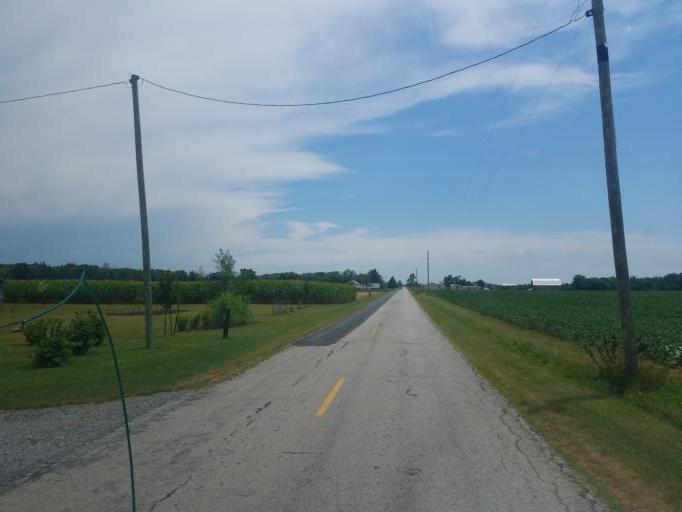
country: US
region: Ohio
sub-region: Paulding County
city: Antwerp
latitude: 41.2333
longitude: -84.7277
